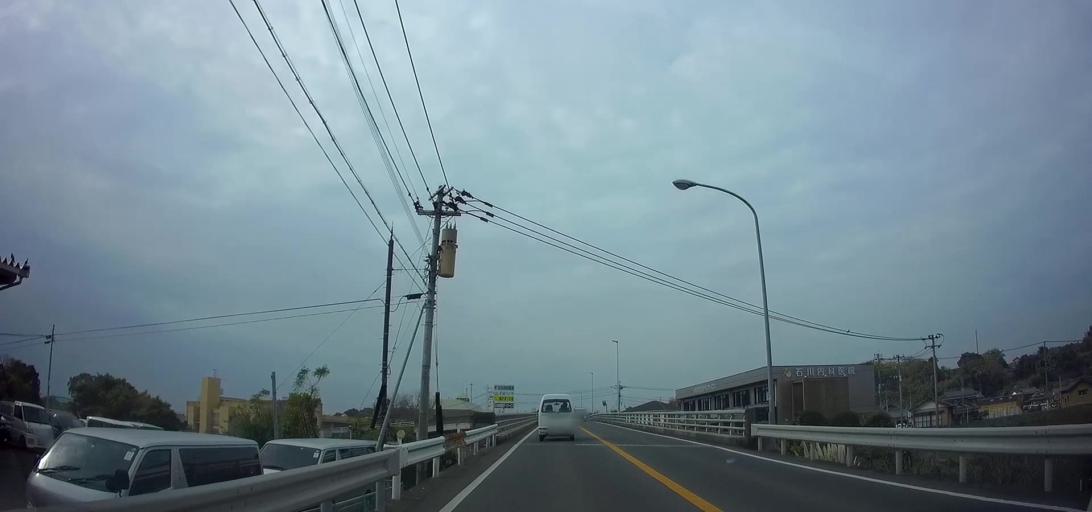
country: JP
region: Nagasaki
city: Shimabara
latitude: 32.6606
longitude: 130.3005
